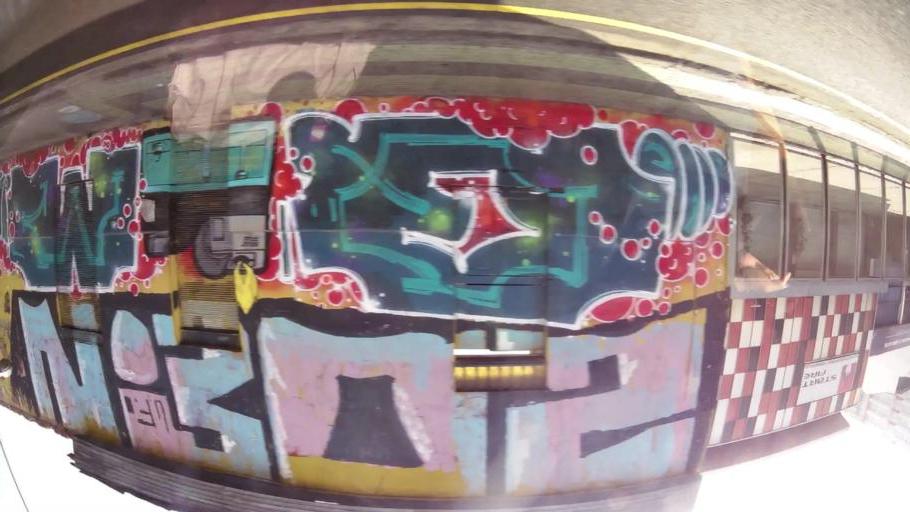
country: CL
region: Santiago Metropolitan
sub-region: Provincia de Santiago
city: Santiago
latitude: -33.4529
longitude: -70.6440
